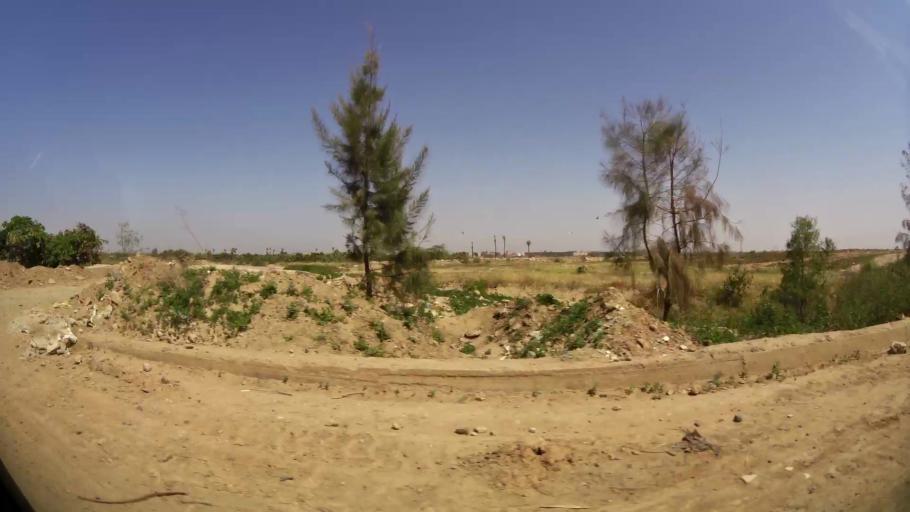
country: MA
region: Souss-Massa-Draa
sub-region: Inezgane-Ait Mellou
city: Inezgane
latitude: 30.3483
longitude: -9.5328
